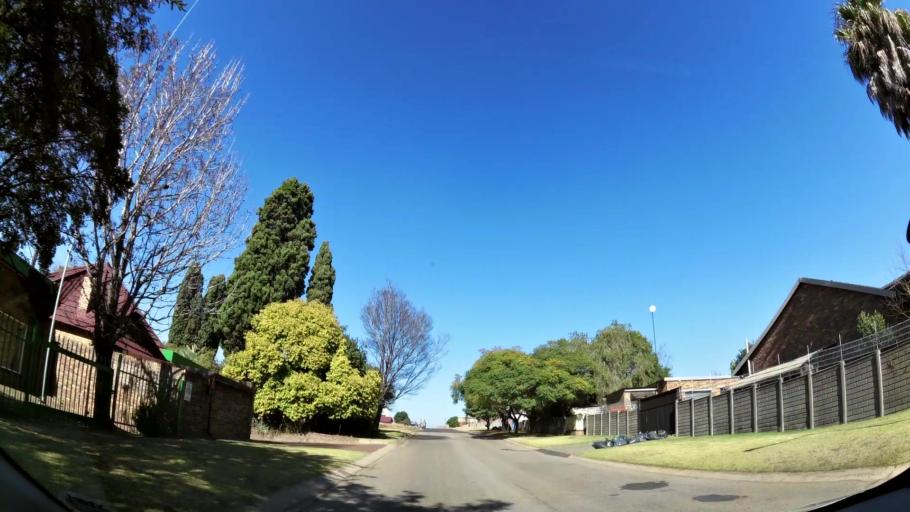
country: ZA
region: Mpumalanga
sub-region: Nkangala District Municipality
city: Witbank
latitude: -25.8707
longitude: 29.2415
